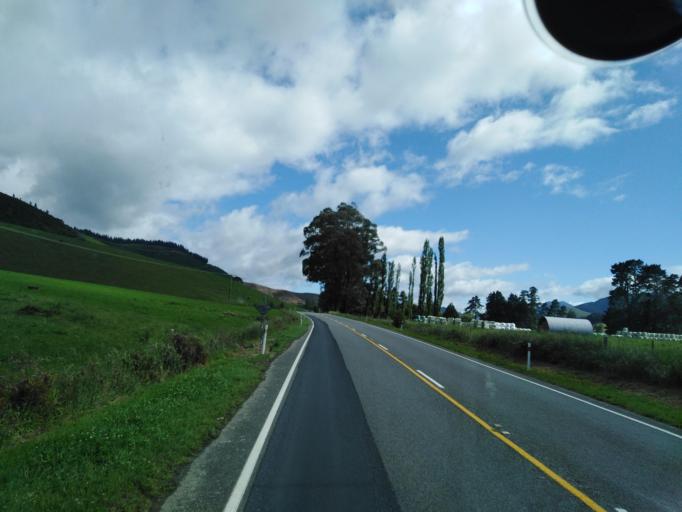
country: NZ
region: Nelson
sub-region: Nelson City
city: Nelson
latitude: -41.2781
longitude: 173.5734
